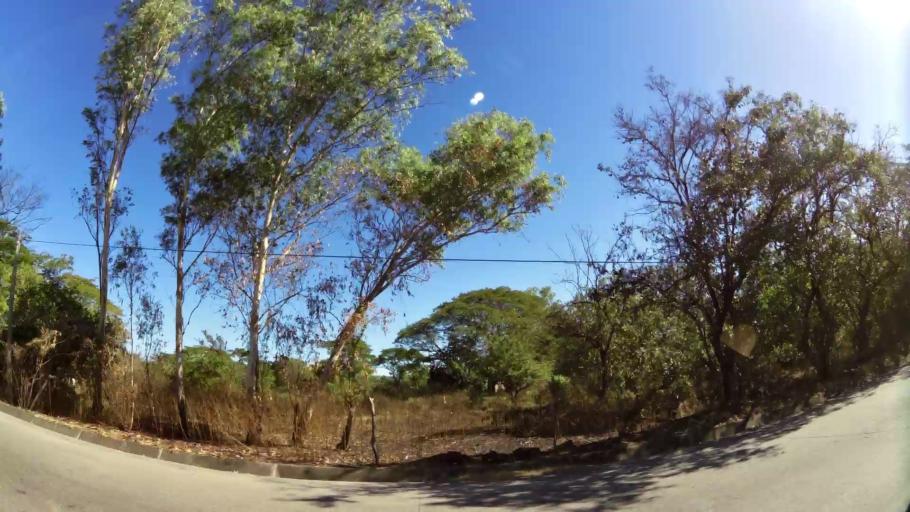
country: SV
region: San Miguel
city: San Miguel
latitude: 13.4502
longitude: -88.1359
